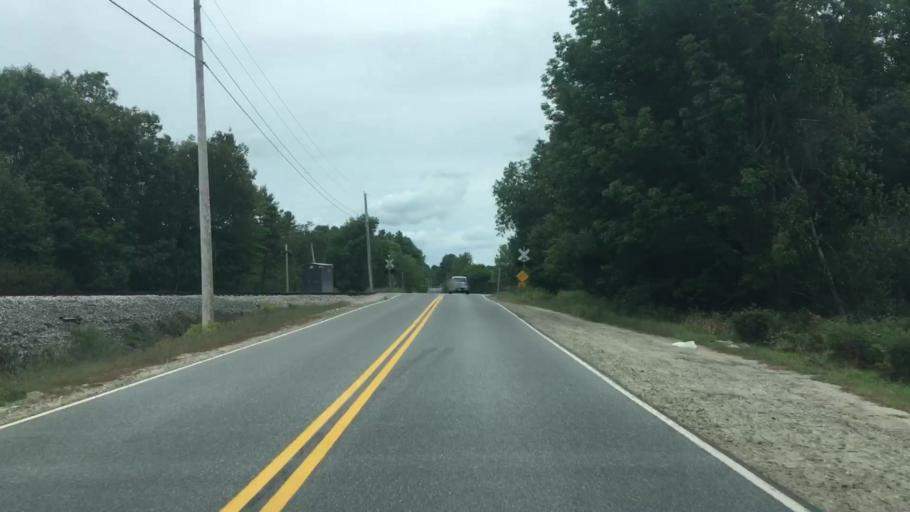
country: US
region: Maine
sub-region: Cumberland County
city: Yarmouth
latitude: 43.8596
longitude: -70.2187
